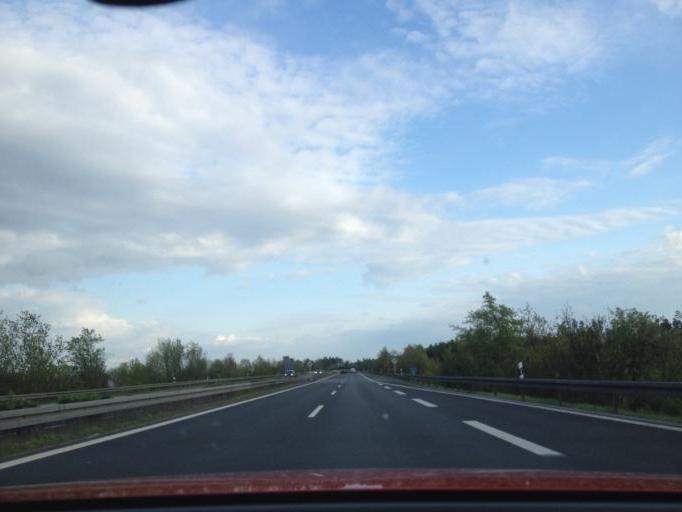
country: DE
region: Bavaria
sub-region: Upper Palatinate
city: Mitterteich
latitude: 49.9346
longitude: 12.2252
